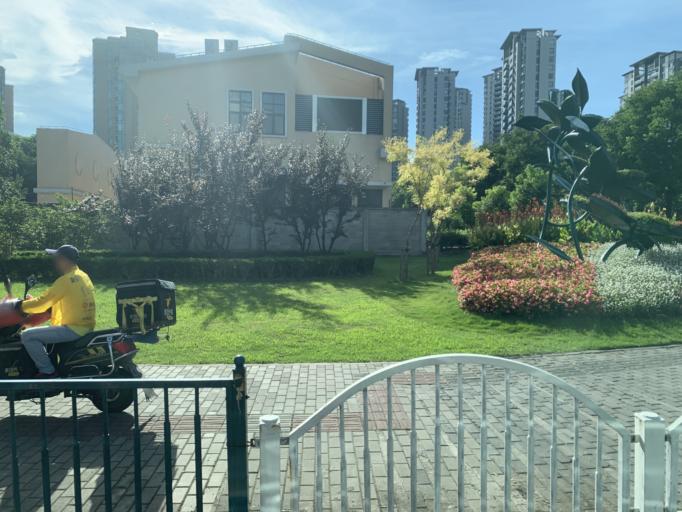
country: CN
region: Shanghai Shi
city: Huamu
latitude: 31.2092
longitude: 121.5323
